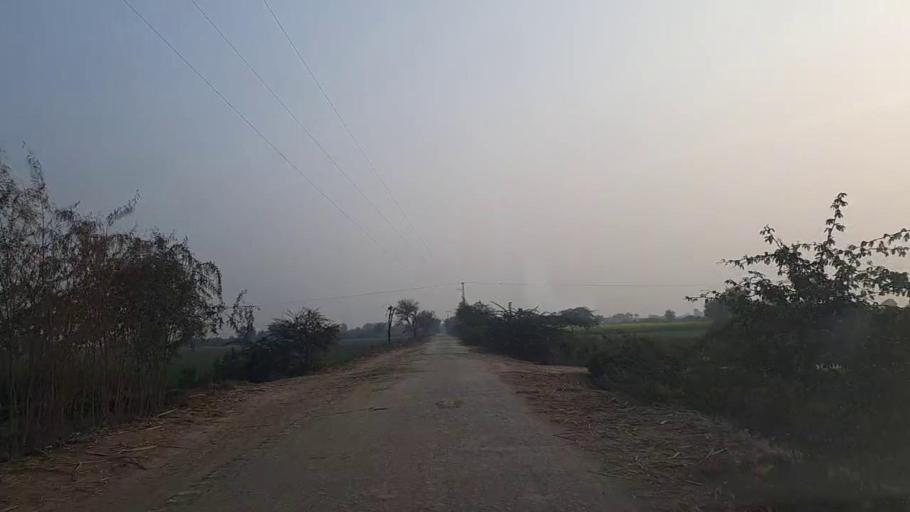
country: PK
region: Sindh
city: Sinjhoro
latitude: 26.1101
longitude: 68.7965
